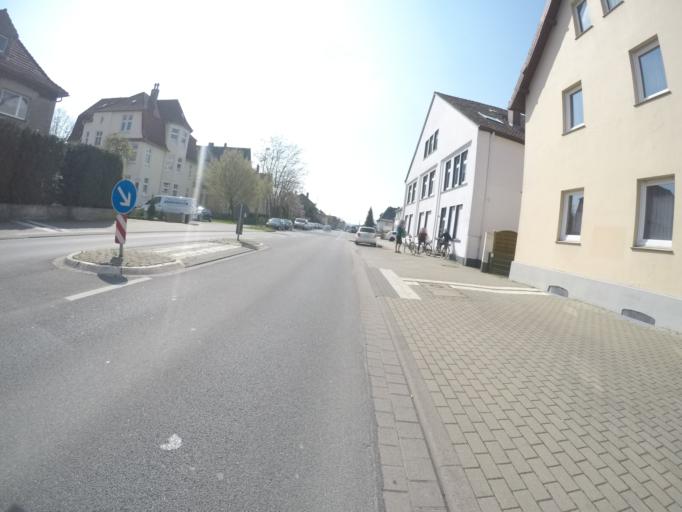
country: DE
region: North Rhine-Westphalia
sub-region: Regierungsbezirk Detmold
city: Bielefeld
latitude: 52.0507
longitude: 8.5464
